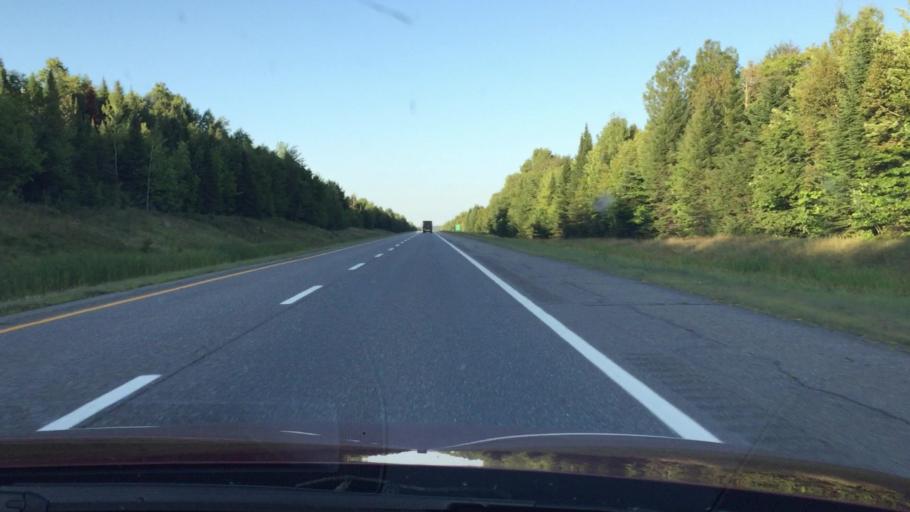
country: US
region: Maine
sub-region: Aroostook County
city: Hodgdon
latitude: 46.1243
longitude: -68.1060
